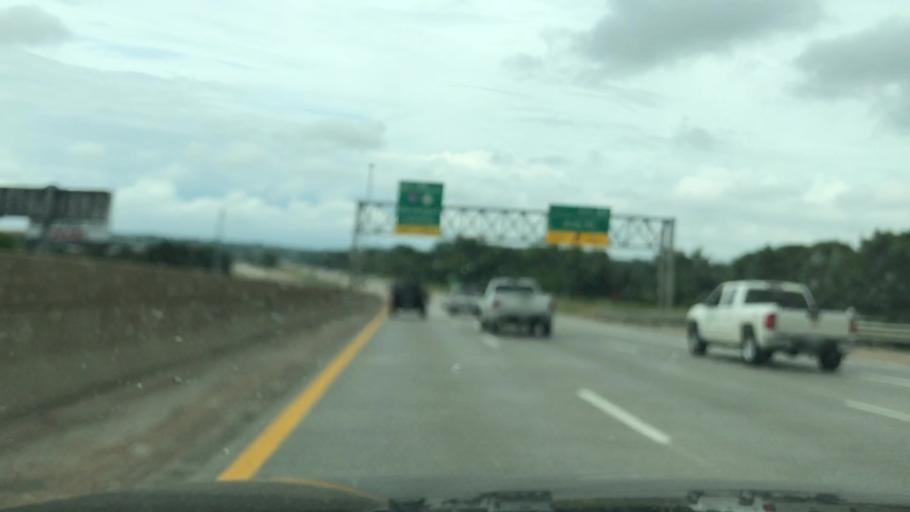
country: US
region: Michigan
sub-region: Kent County
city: Grand Rapids
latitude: 42.9955
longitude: -85.6762
